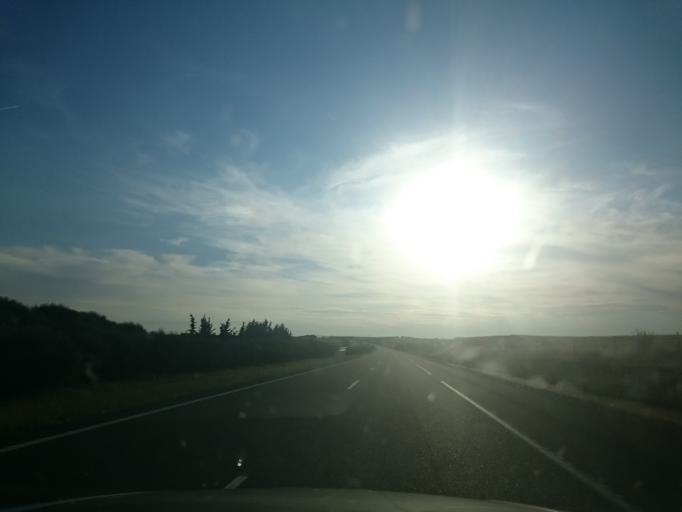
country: ES
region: Castille and Leon
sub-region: Provincia de Palencia
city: Moratinos
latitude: 42.3658
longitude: -4.9493
